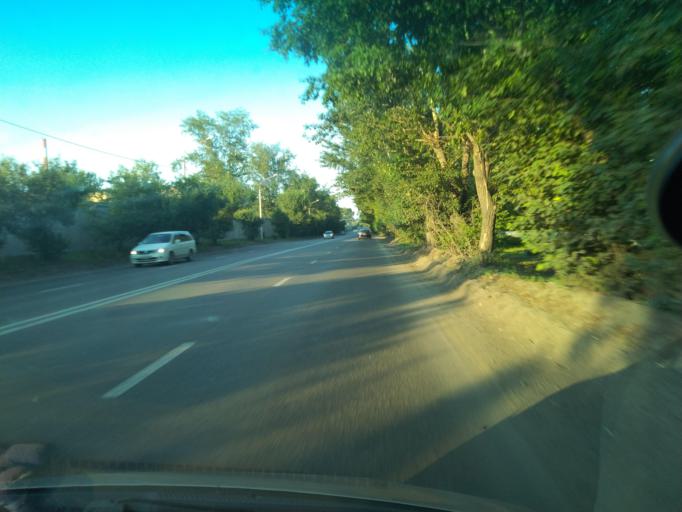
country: RU
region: Krasnoyarskiy
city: Berezovka
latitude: 56.0127
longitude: 93.0149
